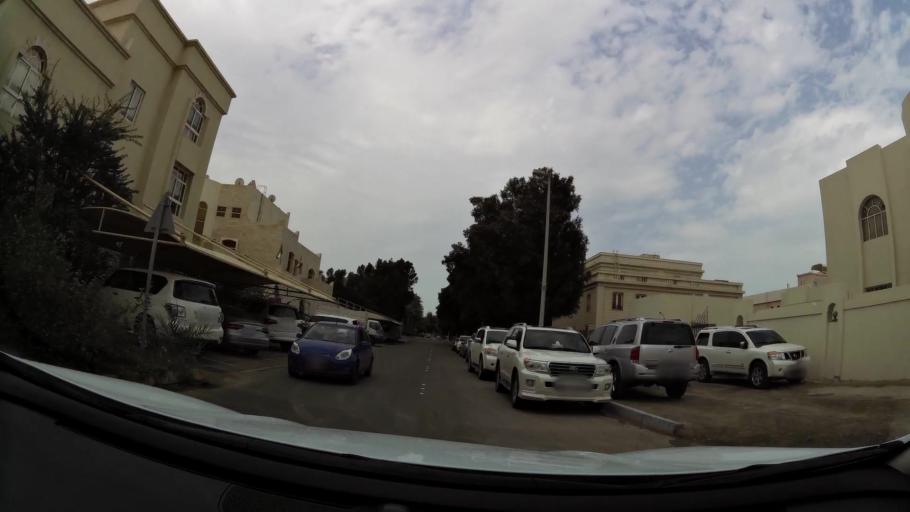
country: AE
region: Abu Dhabi
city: Abu Dhabi
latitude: 24.4352
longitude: 54.4416
